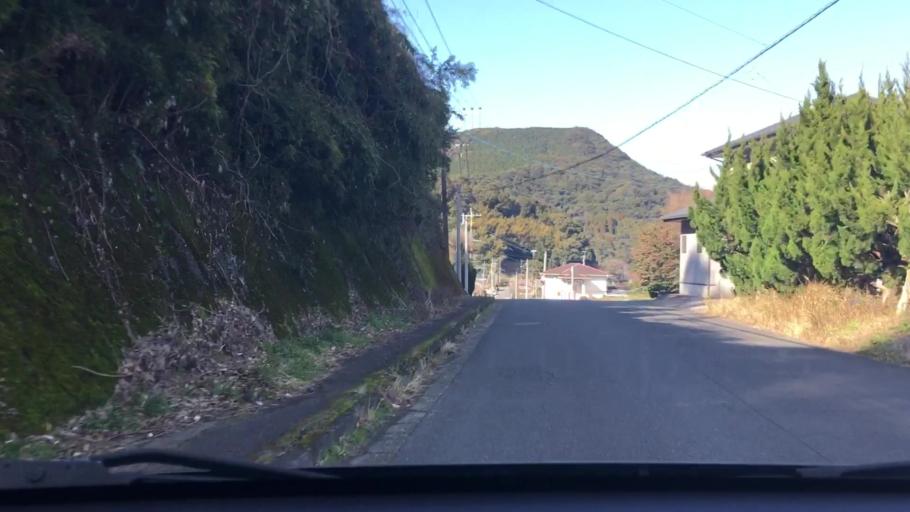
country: JP
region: Kagoshima
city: Ijuin
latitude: 31.7391
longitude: 130.4109
